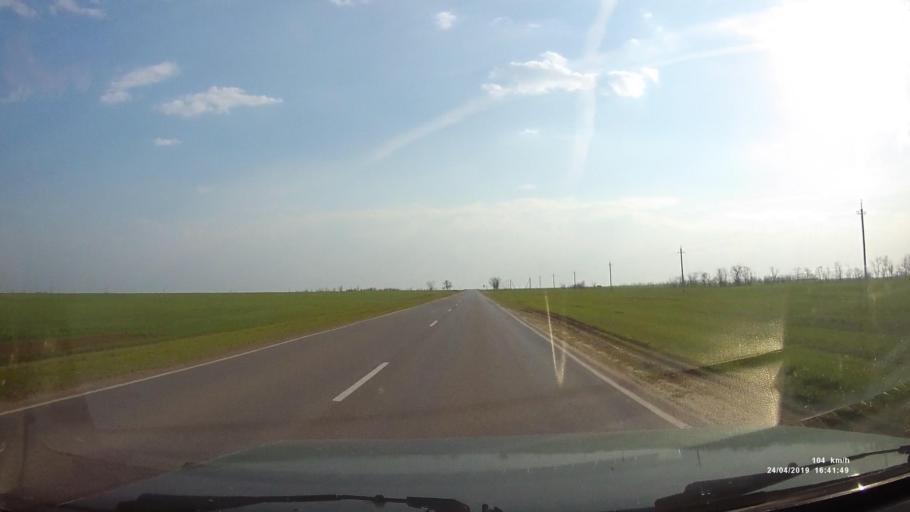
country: RU
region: Rostov
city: Gundorovskiy
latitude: 46.8153
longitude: 41.8624
